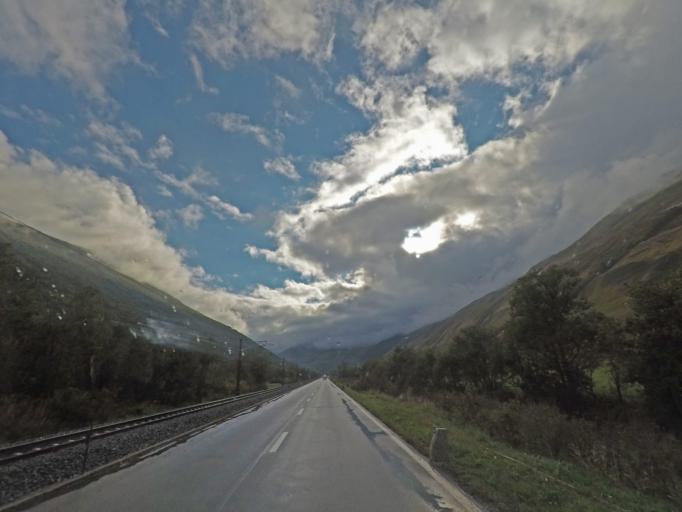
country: CH
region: Uri
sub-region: Uri
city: Andermatt
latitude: 46.6092
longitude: 8.5322
